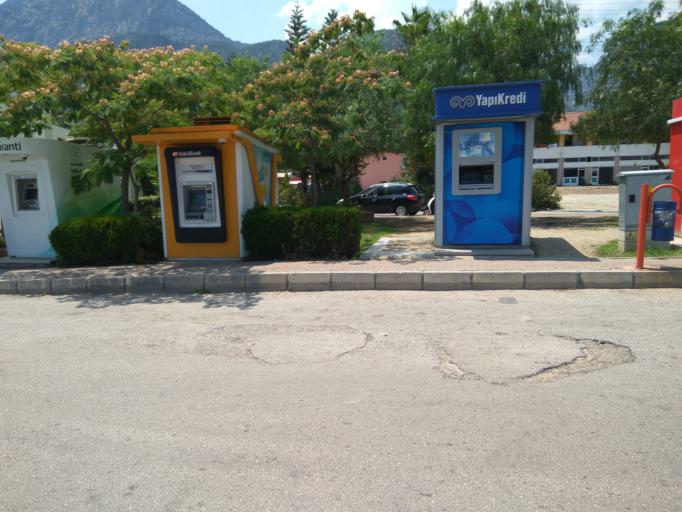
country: TR
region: Antalya
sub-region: Kemer
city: Goeynuek
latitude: 36.6674
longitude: 30.5517
